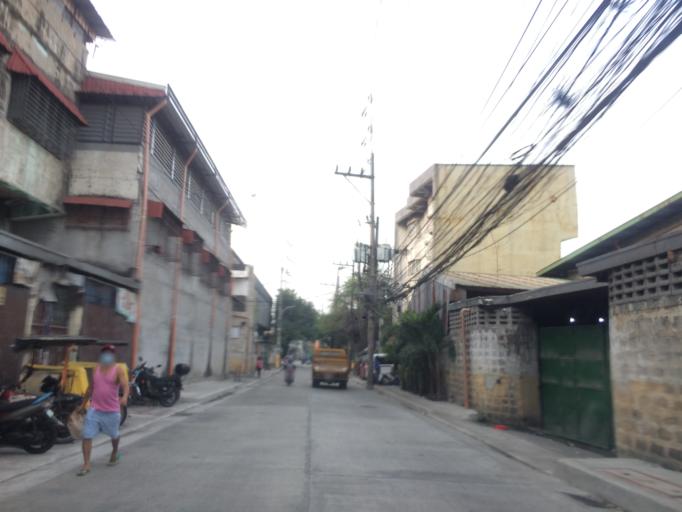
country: PH
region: Calabarzon
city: Del Monte
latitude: 14.6503
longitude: 121.0097
